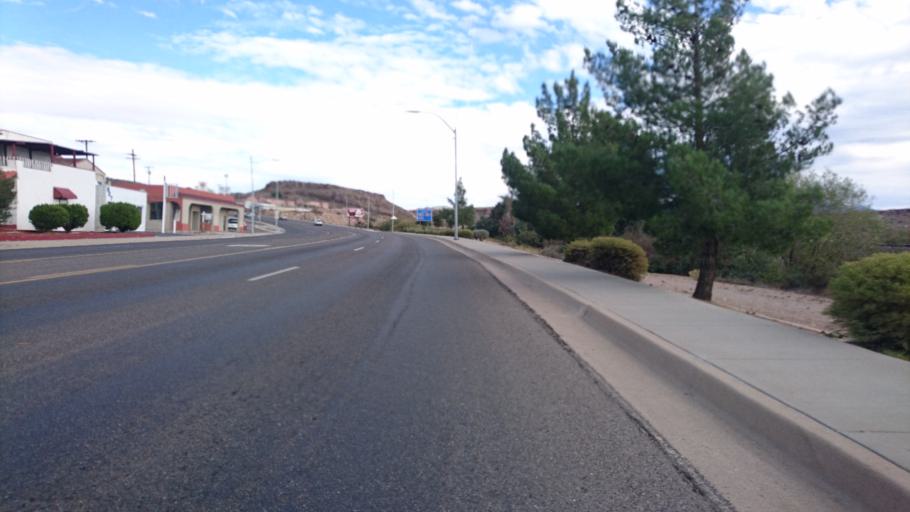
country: US
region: Arizona
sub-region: Mohave County
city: Kingman
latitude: 35.1866
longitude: -114.0433
